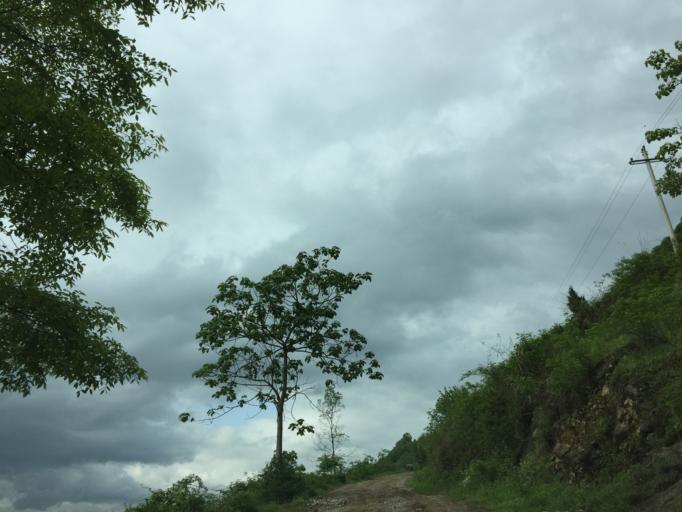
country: CN
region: Guizhou Sheng
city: Xujiaba
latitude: 27.8473
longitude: 108.2171
